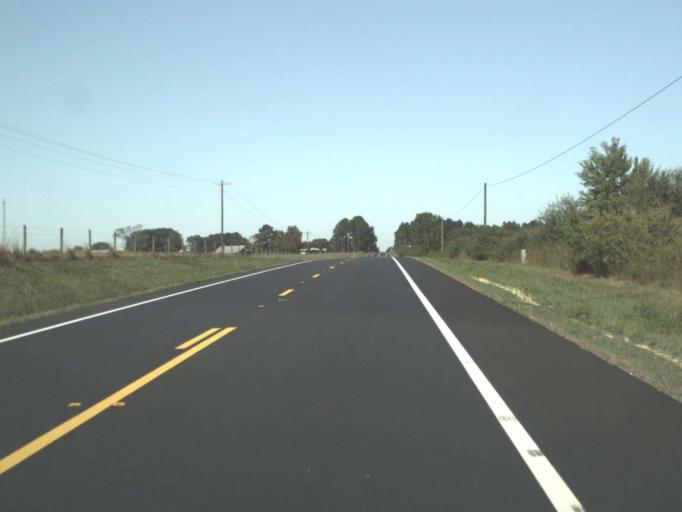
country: US
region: Florida
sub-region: Walton County
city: DeFuniak Springs
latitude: 30.8458
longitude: -86.2408
